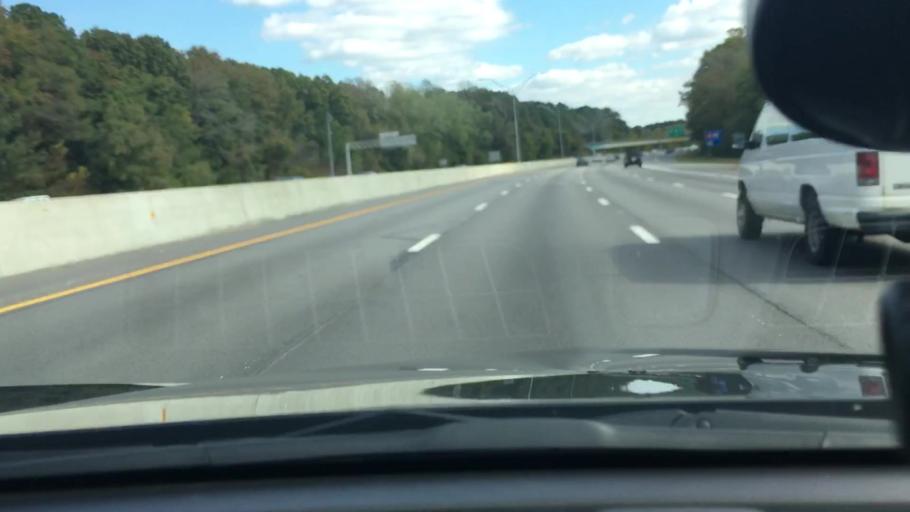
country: US
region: North Carolina
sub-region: Wake County
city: Raleigh
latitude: 35.7570
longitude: -78.6625
